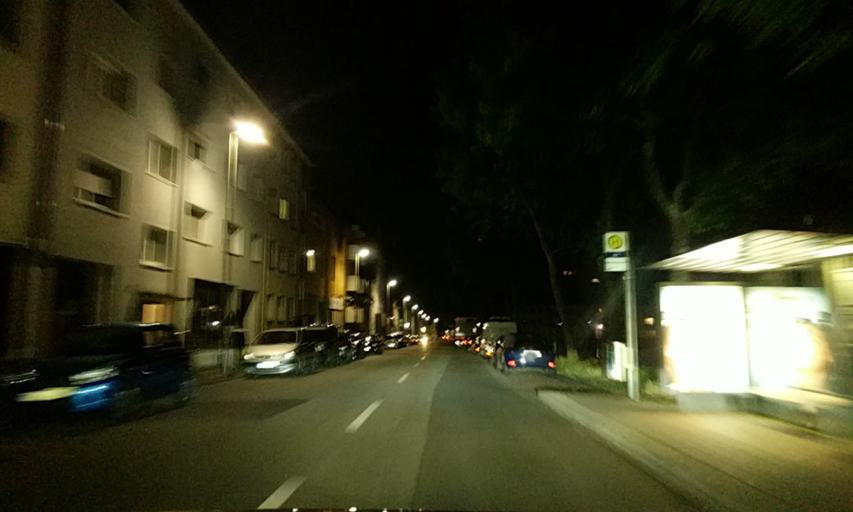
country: DE
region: Rheinland-Pfalz
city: Kaiserslautern
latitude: 49.4501
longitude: 7.7885
